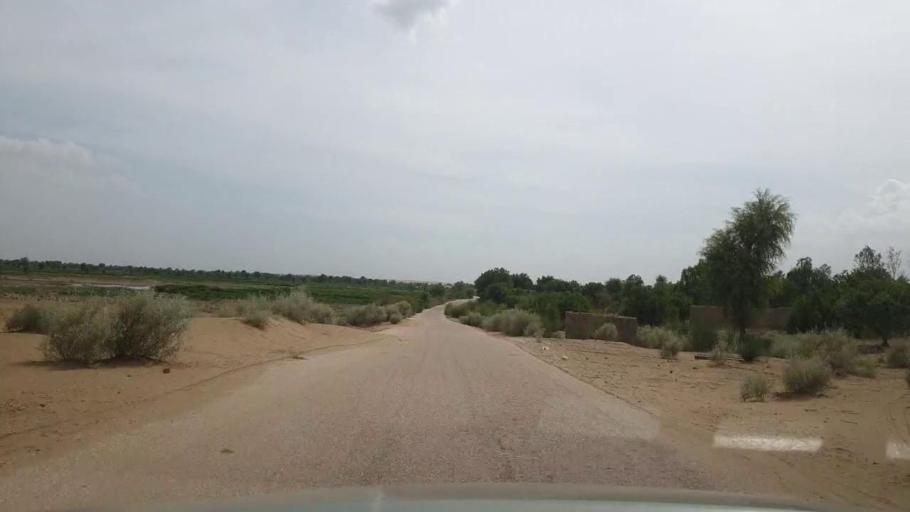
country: PK
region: Sindh
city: Kot Diji
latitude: 27.1493
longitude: 69.0316
